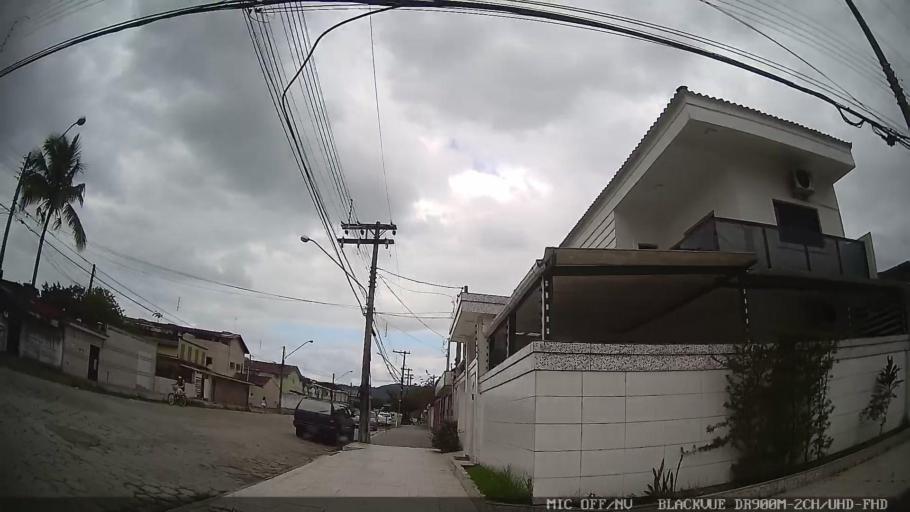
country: BR
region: Sao Paulo
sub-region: Guaruja
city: Guaruja
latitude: -23.9953
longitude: -46.2779
